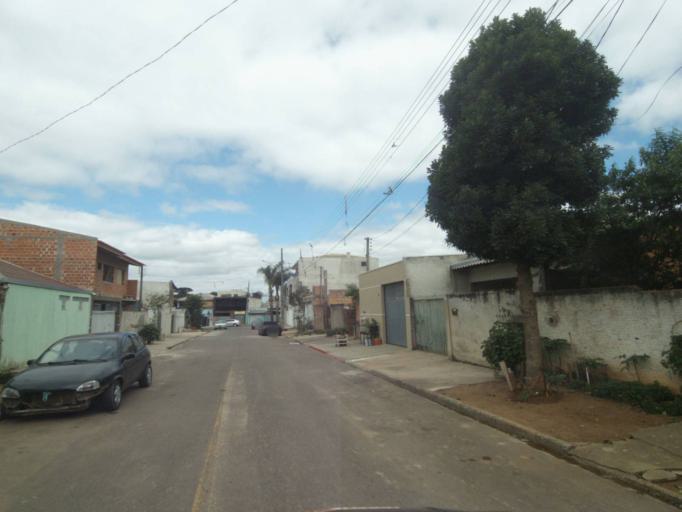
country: BR
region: Parana
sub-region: Sao Jose Dos Pinhais
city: Sao Jose dos Pinhais
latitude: -25.5544
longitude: -49.2655
